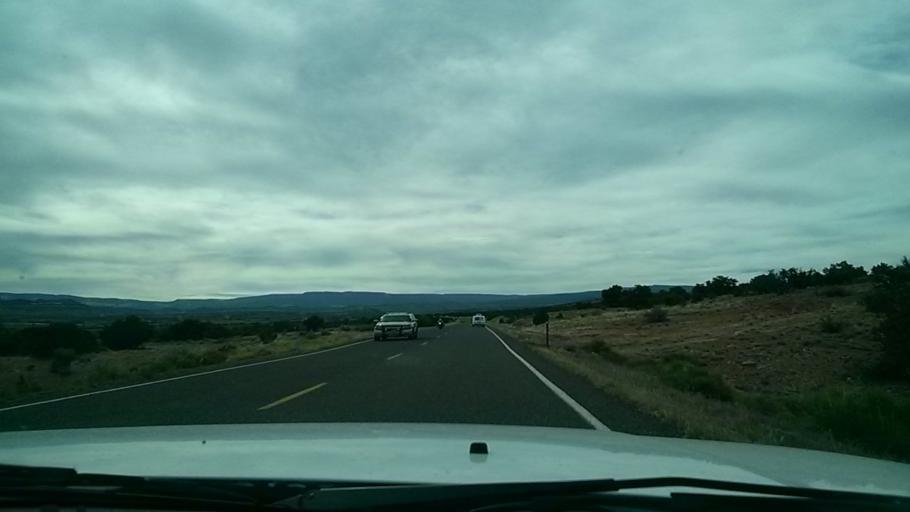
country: US
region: Utah
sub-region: Wayne County
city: Loa
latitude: 37.7329
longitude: -111.5395
